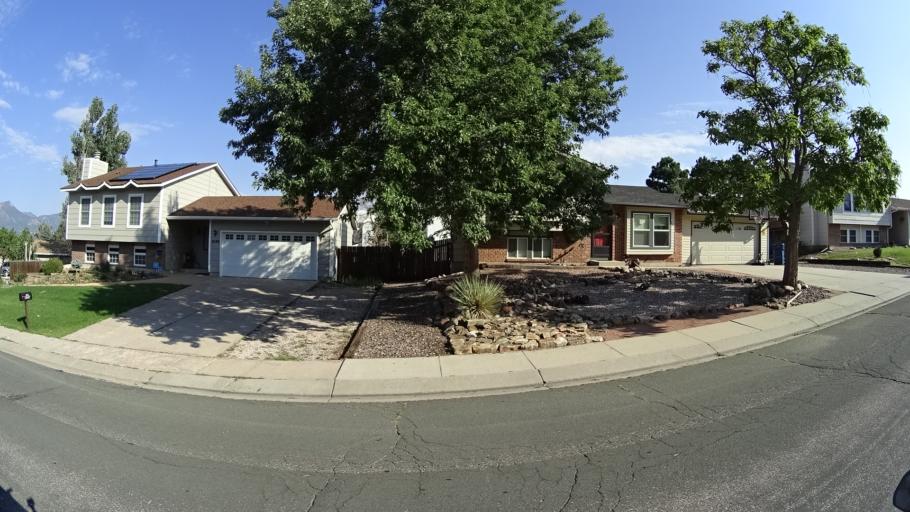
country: US
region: Colorado
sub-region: El Paso County
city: Air Force Academy
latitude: 38.9458
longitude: -104.7787
